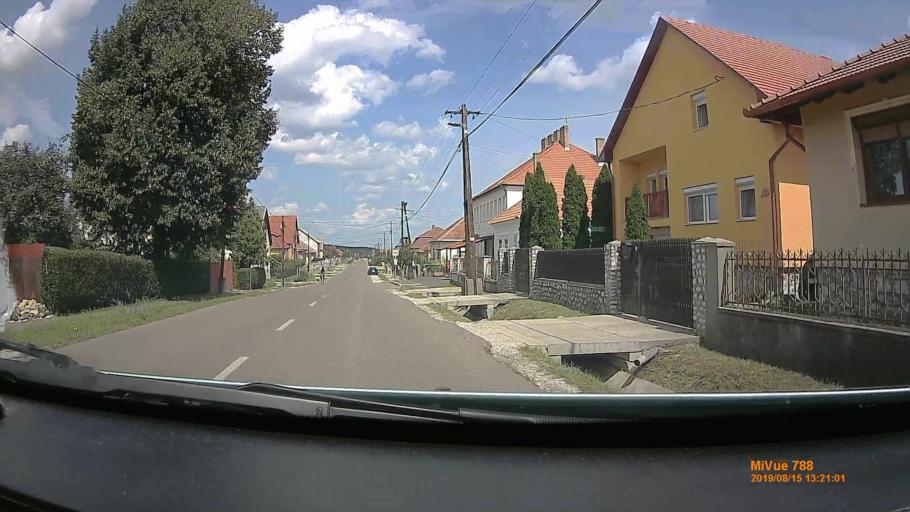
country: HU
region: Borsod-Abauj-Zemplen
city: Kazincbarcika
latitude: 48.1786
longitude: 20.6394
